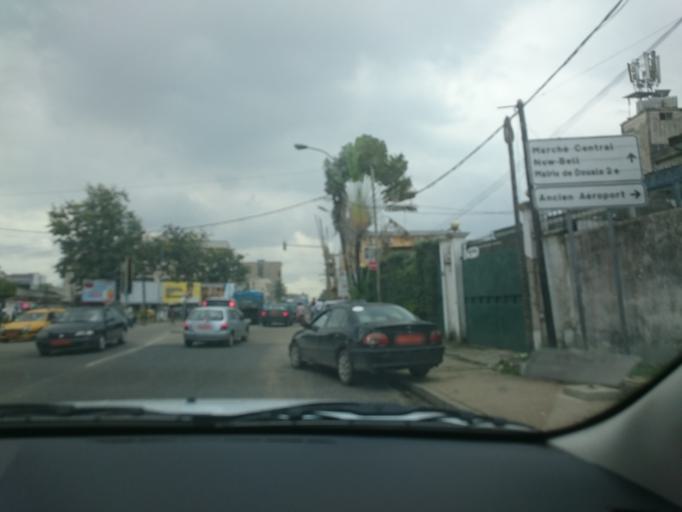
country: CM
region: Littoral
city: Douala
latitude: 4.0193
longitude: 9.7007
